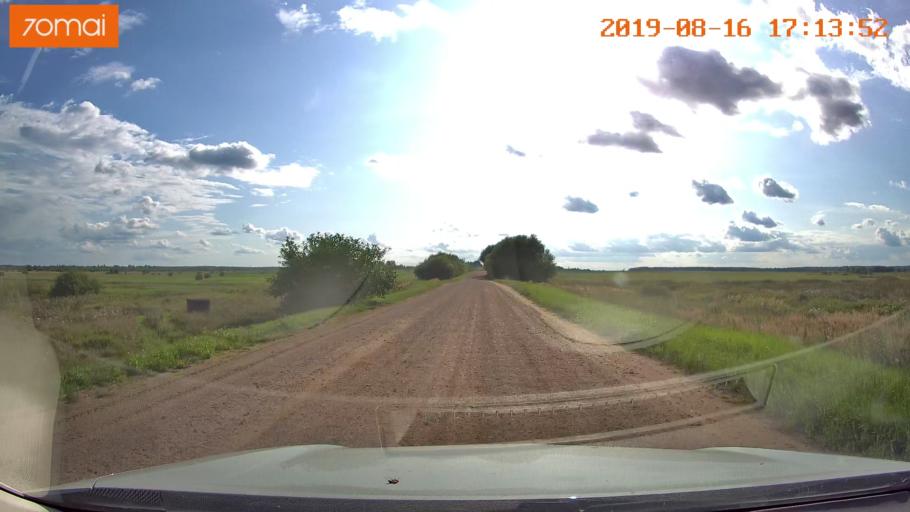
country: BY
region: Mogilev
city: Hlusha
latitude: 53.1874
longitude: 28.8685
